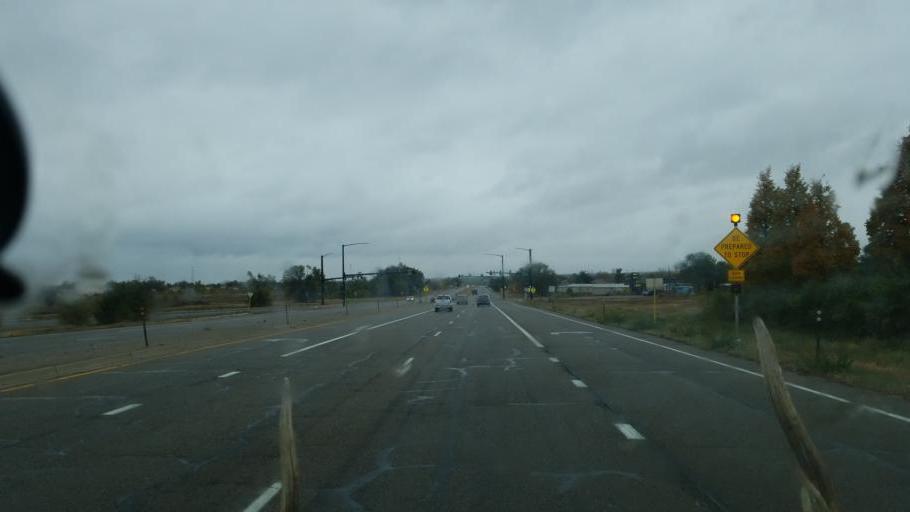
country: US
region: Colorado
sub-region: Pueblo County
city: Pueblo
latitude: 38.2841
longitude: -104.5753
